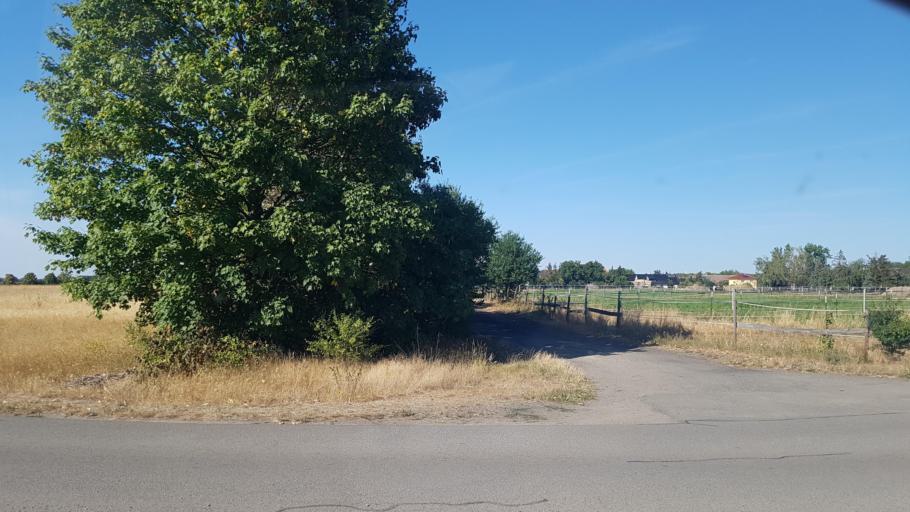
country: DE
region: Brandenburg
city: Muhlberg
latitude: 51.4737
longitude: 13.2662
